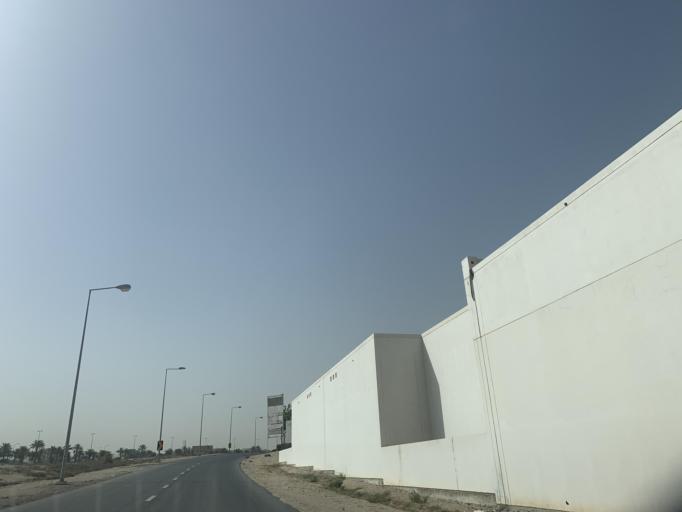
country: BH
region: Northern
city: Ar Rifa'
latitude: 26.1468
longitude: 50.5381
